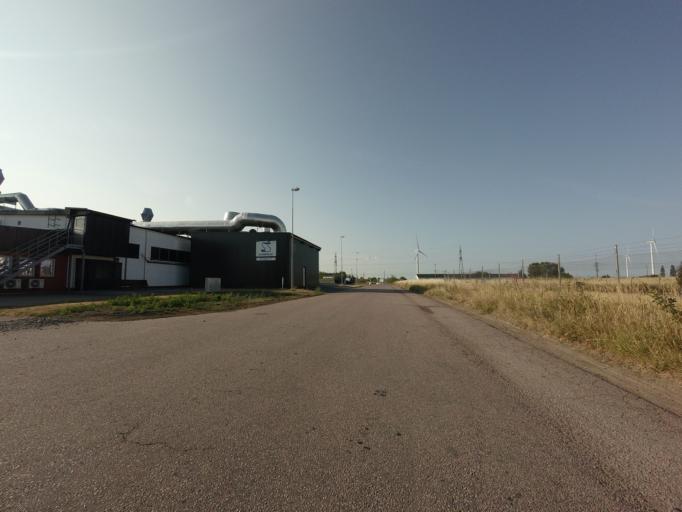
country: SE
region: Skane
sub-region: Landskrona
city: Landskrona
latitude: 55.8684
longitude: 12.8749
